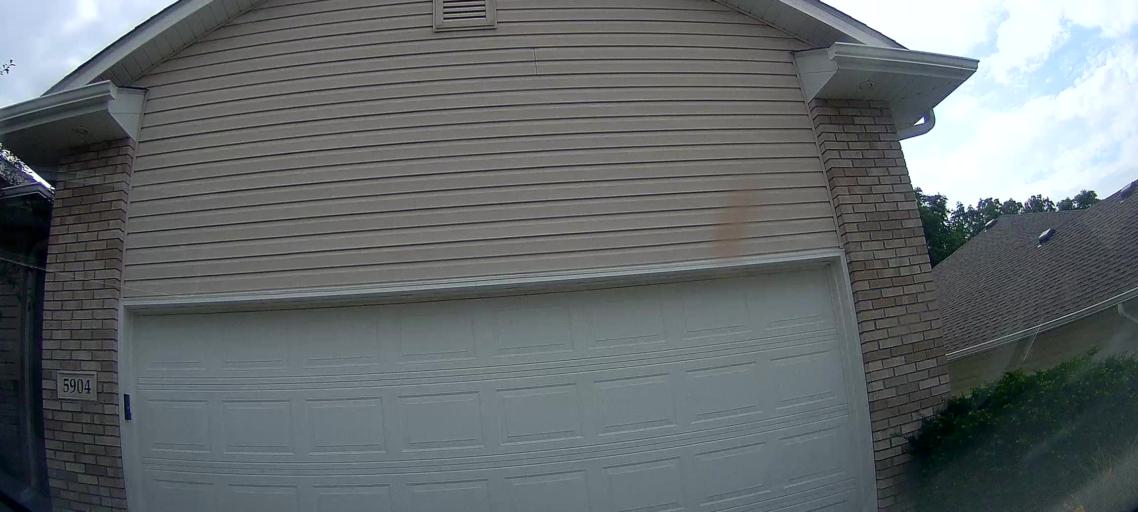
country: US
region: Nebraska
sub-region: Douglas County
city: Ralston
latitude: 41.3118
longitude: -96.0568
